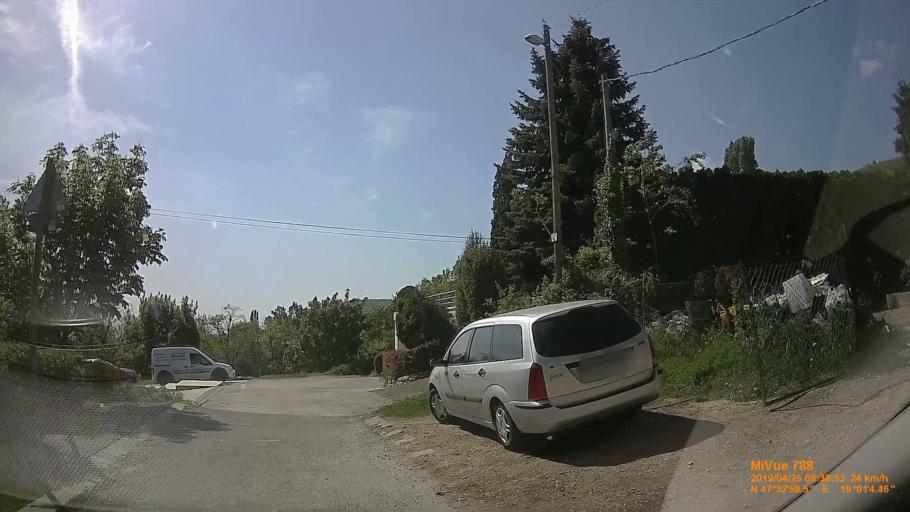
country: HU
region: Budapest
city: Budapest III. keruelet
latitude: 47.5499
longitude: 19.0179
